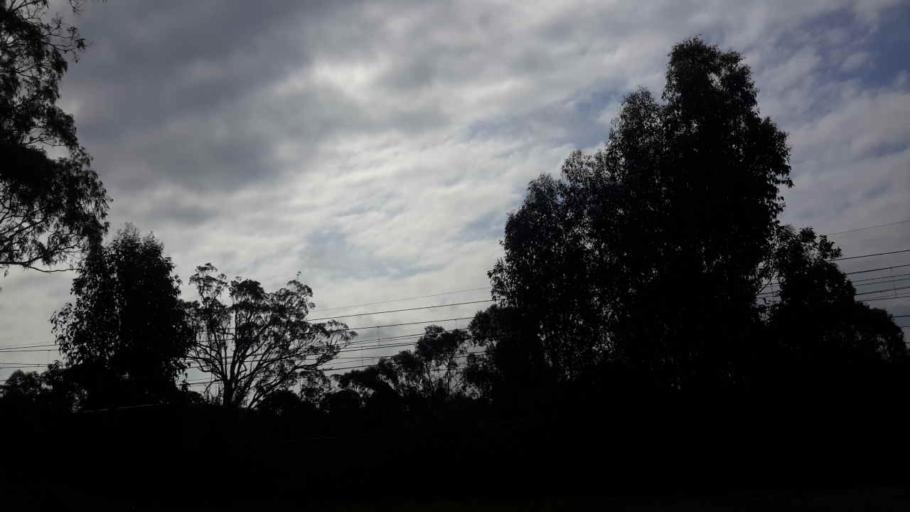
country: AU
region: New South Wales
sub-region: Campbelltown Municipality
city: Glen Alpine
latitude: -34.0785
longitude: 150.7836
